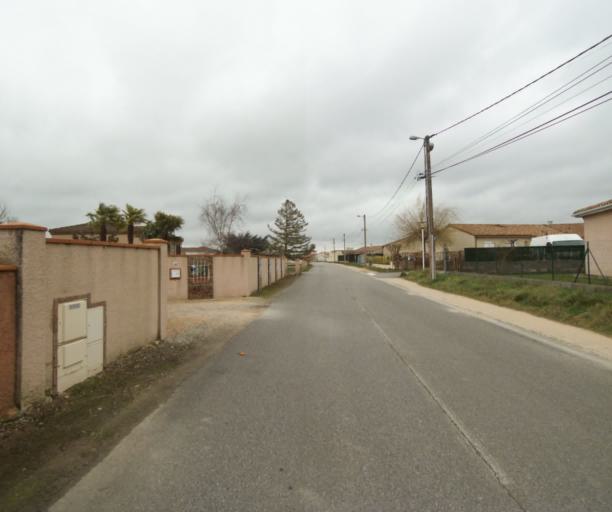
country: FR
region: Midi-Pyrenees
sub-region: Departement de l'Ariege
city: Mazeres
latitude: 43.2458
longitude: 1.6800
